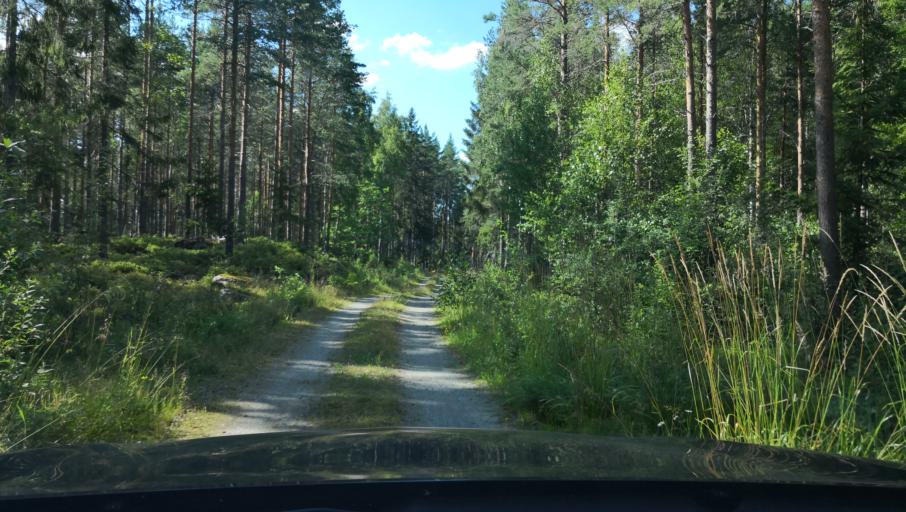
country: SE
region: Vaestmanland
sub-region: Vasteras
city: Skultuna
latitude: 59.7129
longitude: 16.3693
